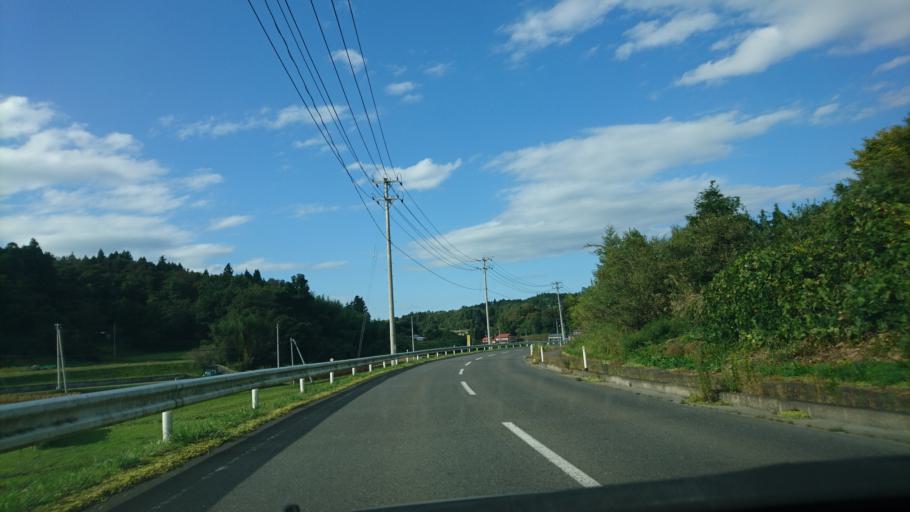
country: JP
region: Iwate
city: Ichinoseki
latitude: 38.8893
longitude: 141.3317
